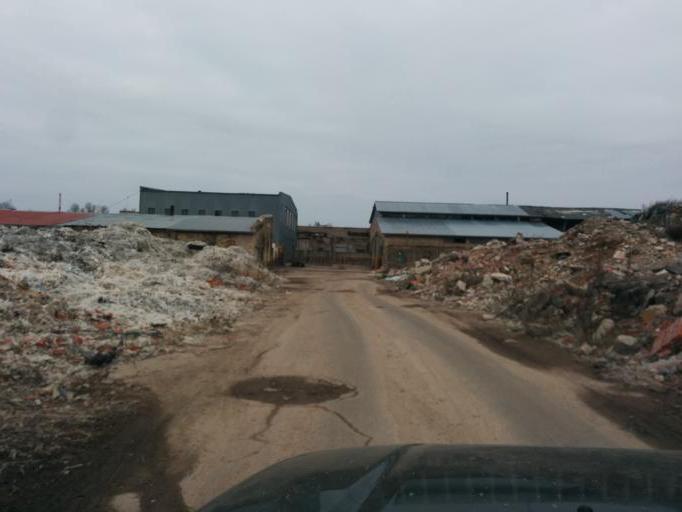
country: LV
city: Tireli
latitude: 56.9443
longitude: 23.6353
